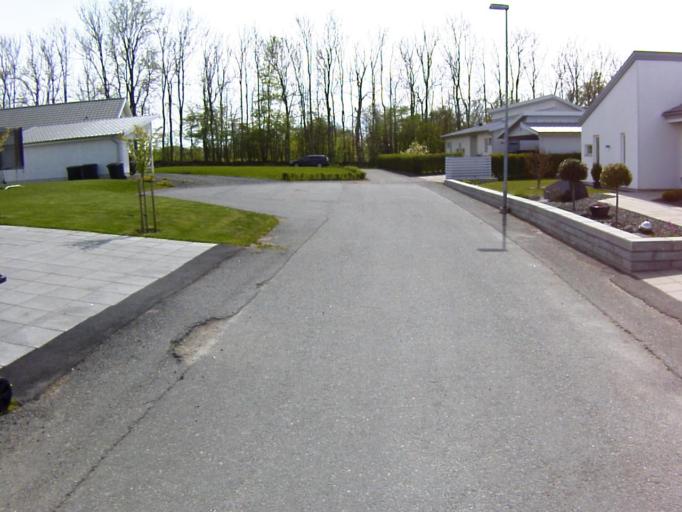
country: SE
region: Skane
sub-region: Kristianstads Kommun
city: Fjalkinge
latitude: 56.0923
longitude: 14.2356
